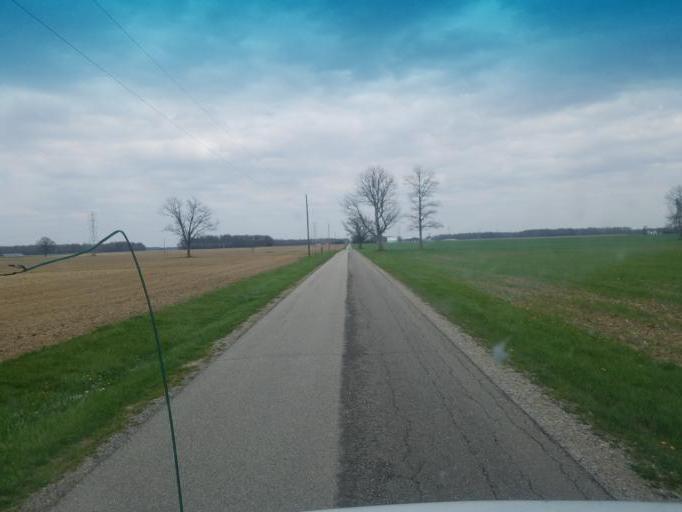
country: US
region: Ohio
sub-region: Crawford County
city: Bucyrus
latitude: 40.9795
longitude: -82.9890
